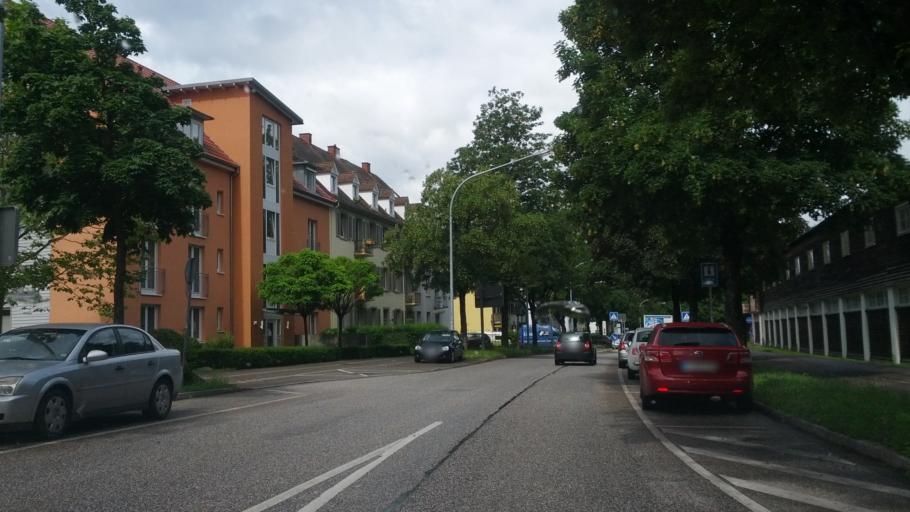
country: DE
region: Baden-Wuerttemberg
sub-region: Freiburg Region
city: Freiburg
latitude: 47.9872
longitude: 7.8959
